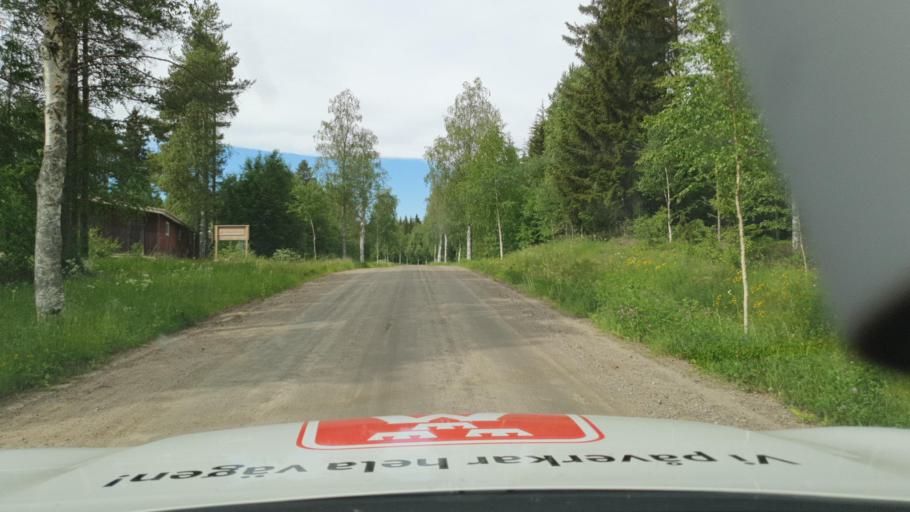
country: SE
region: Vaesterbotten
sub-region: Skelleftea Kommun
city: Burtraesk
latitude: 64.4586
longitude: 20.4723
